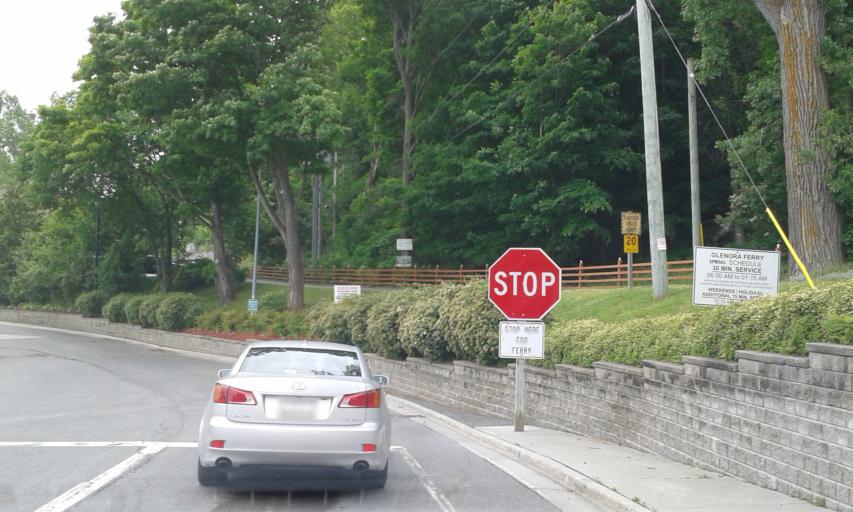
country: CA
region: Ontario
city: Picton
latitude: 44.0416
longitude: -77.0600
